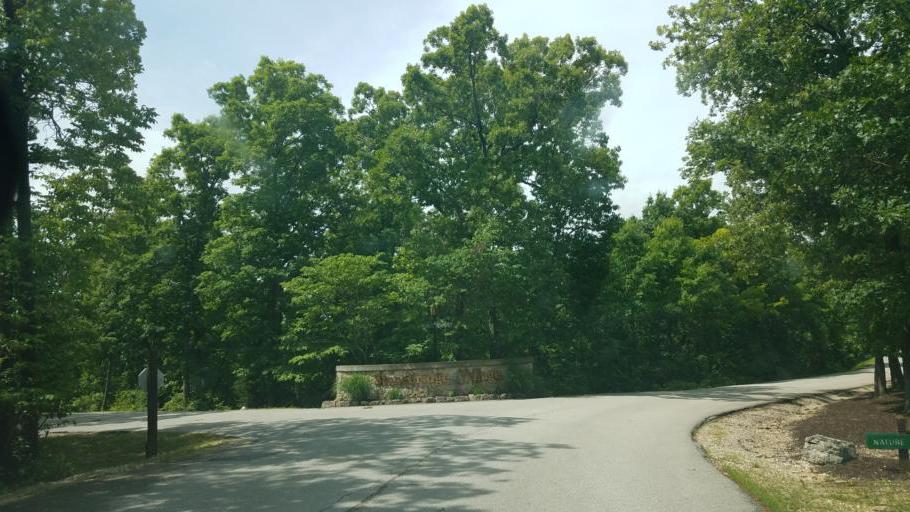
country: US
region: Missouri
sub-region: Camden County
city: Osage Beach
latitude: 38.1566
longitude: -92.6795
